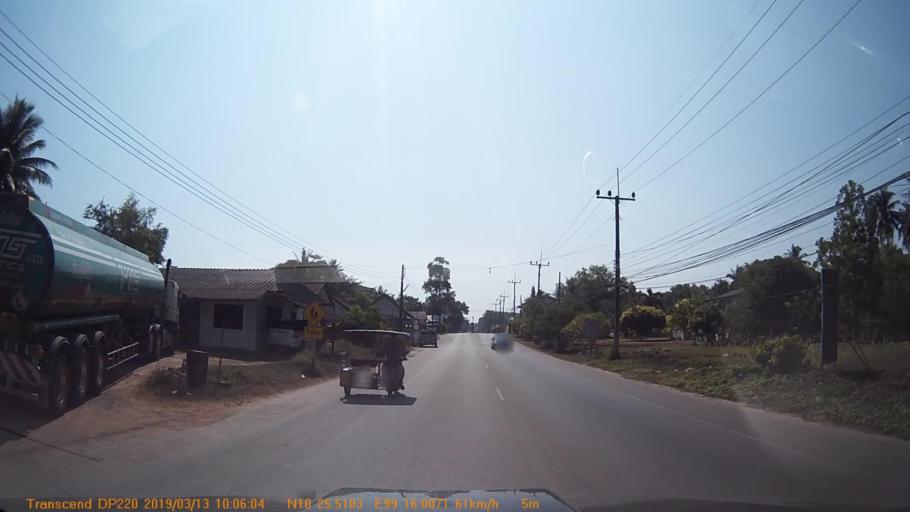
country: TH
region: Chumphon
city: Chumphon
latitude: 10.4250
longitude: 99.2670
